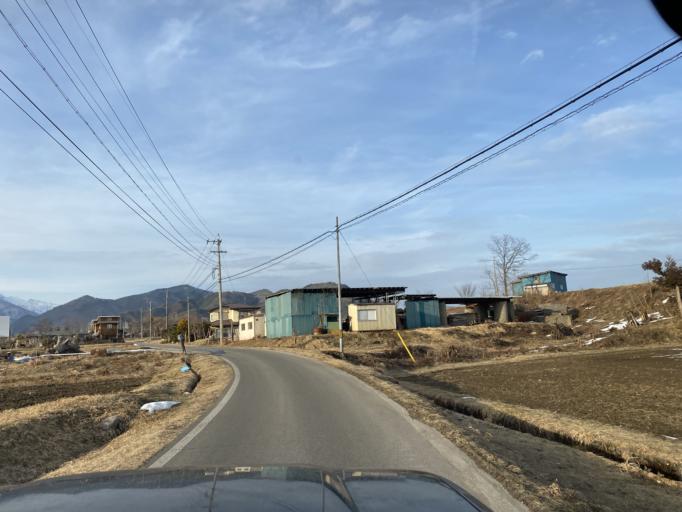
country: JP
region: Nagano
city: Omachi
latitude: 36.5142
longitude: 137.8218
